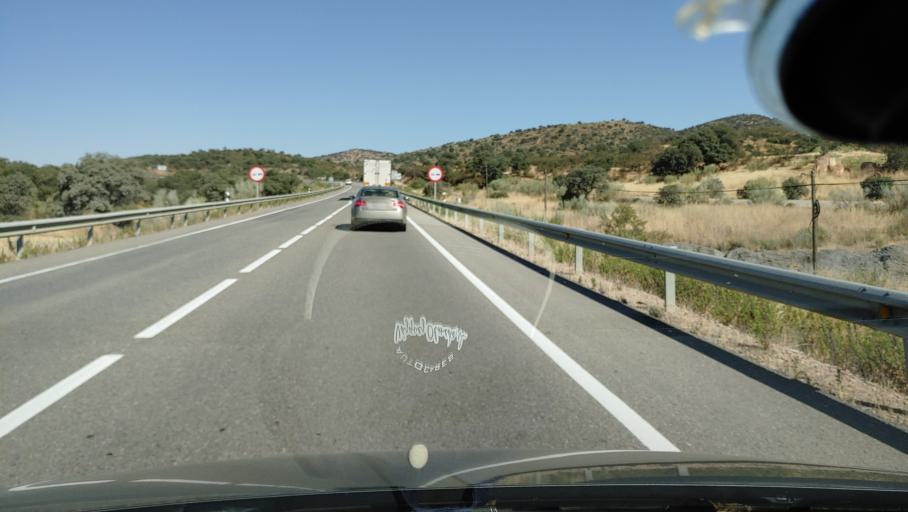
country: ES
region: Andalusia
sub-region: Province of Cordoba
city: Espiel
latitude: 38.1660
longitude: -4.9908
